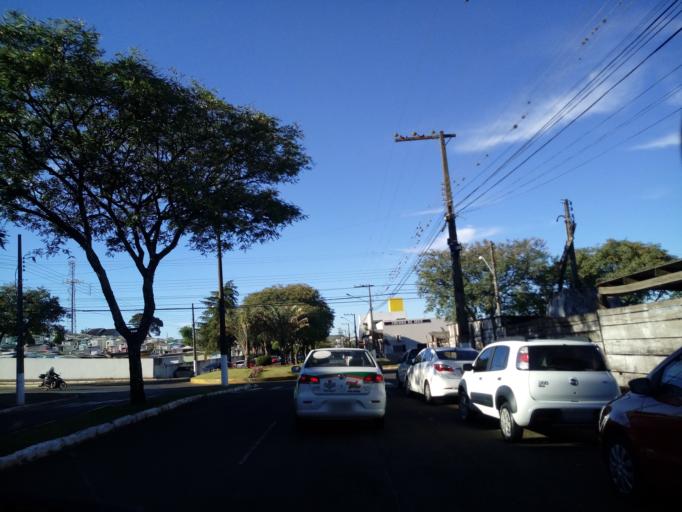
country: BR
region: Santa Catarina
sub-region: Chapeco
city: Chapeco
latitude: -27.1117
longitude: -52.6145
